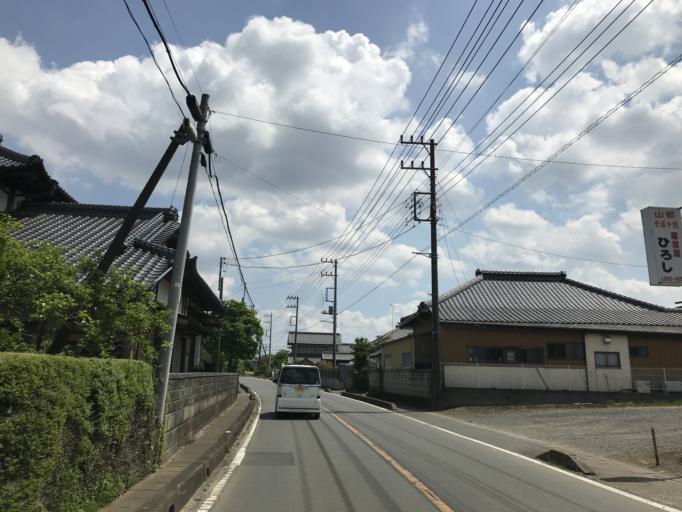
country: JP
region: Ibaraki
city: Mitsukaido
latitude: 36.0534
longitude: 140.0384
